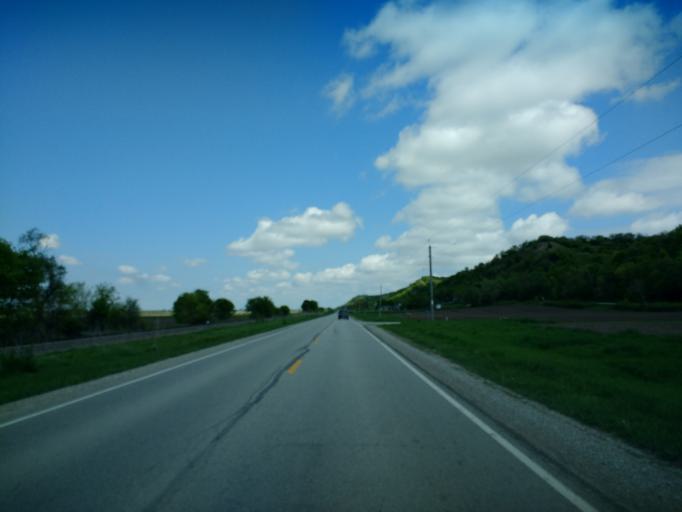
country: US
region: Iowa
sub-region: Harrison County
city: Missouri Valley
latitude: 41.4645
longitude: -95.8780
